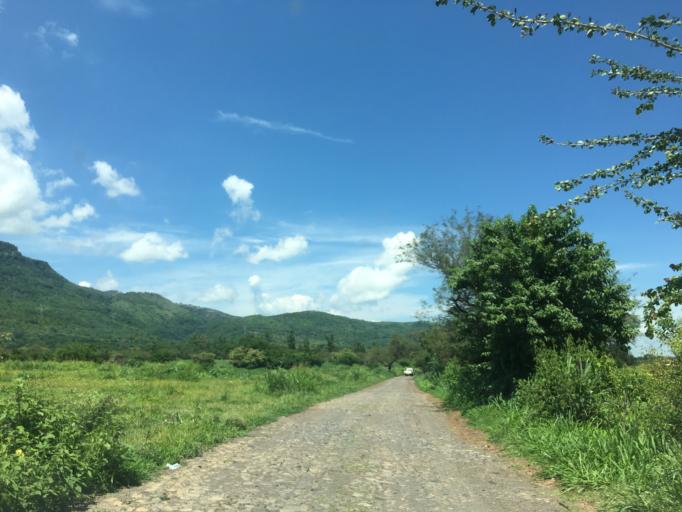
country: MX
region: Nayarit
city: Ixtlan del Rio
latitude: 21.0369
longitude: -104.3493
